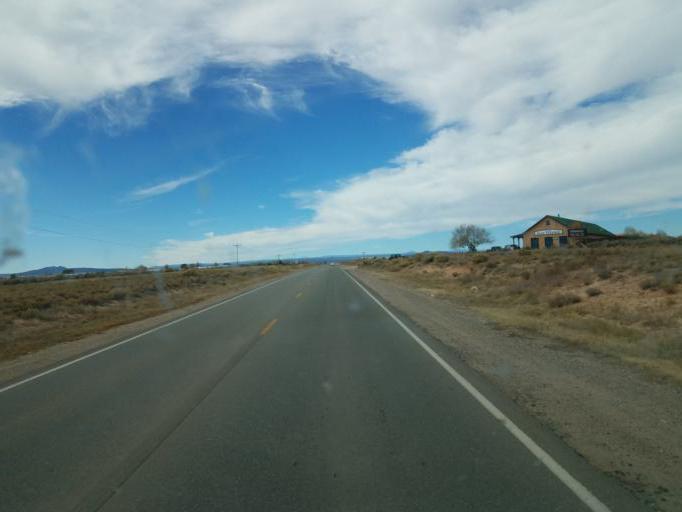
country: US
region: New Mexico
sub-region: Taos County
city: Taos
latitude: 36.4593
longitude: -105.6299
